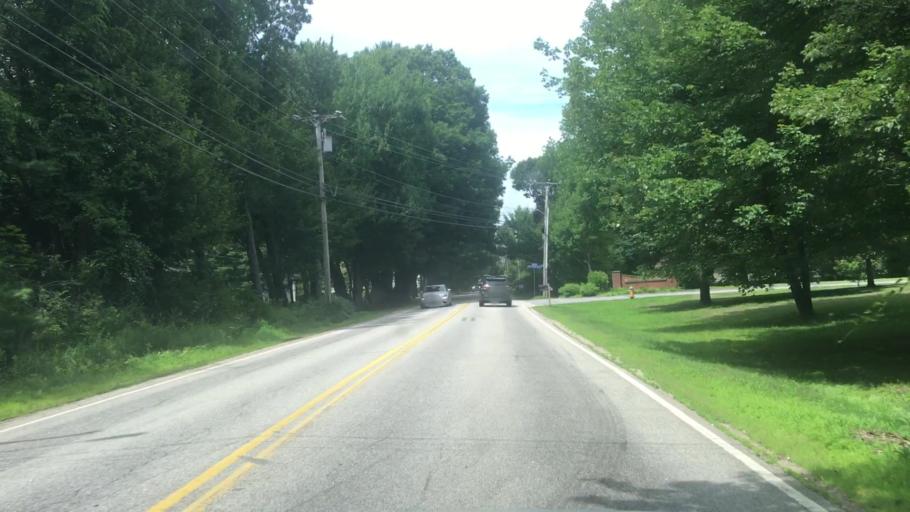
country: US
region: Maine
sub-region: Cumberland County
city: Scarborough
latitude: 43.5843
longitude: -70.2923
